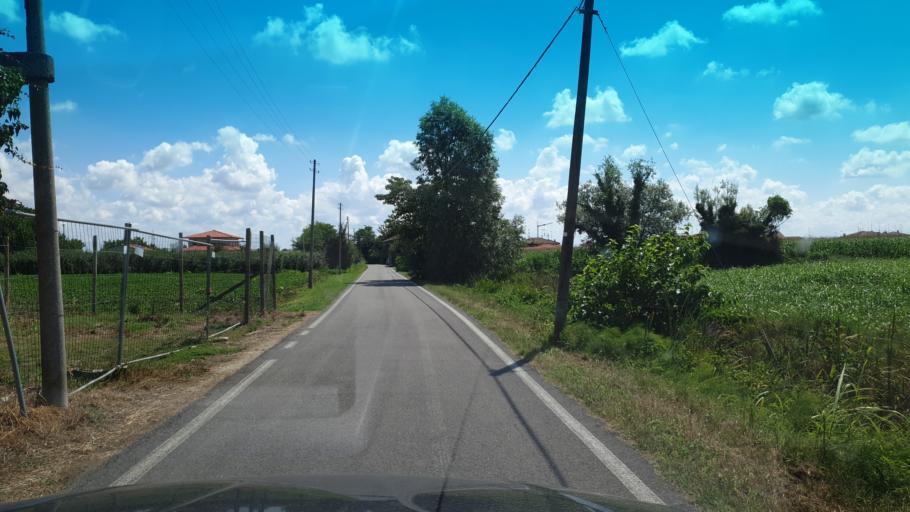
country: IT
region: Veneto
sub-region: Provincia di Rovigo
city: Fratta Polesine
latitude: 45.0334
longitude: 11.6456
